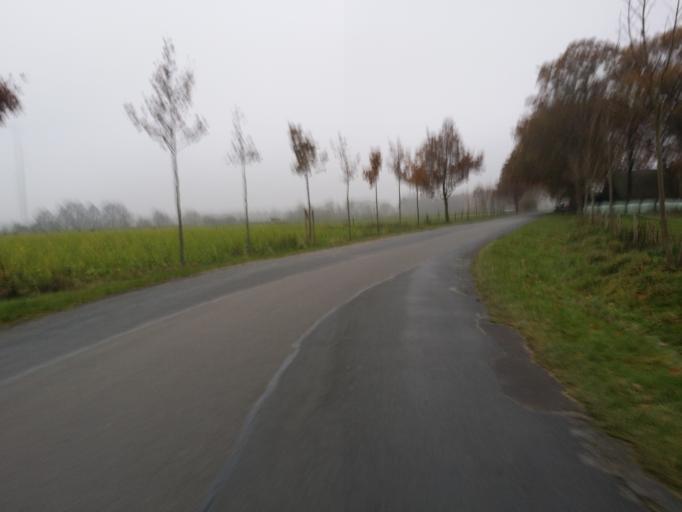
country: DE
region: Lower Saxony
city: Delmenhorst
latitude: 53.0167
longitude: 8.6217
